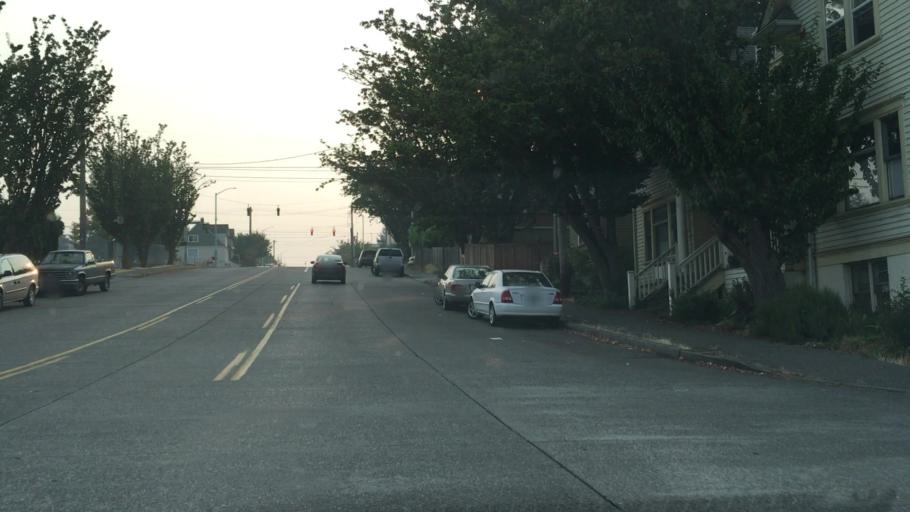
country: US
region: Washington
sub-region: Pierce County
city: Tacoma
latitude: 47.2485
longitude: -122.4450
